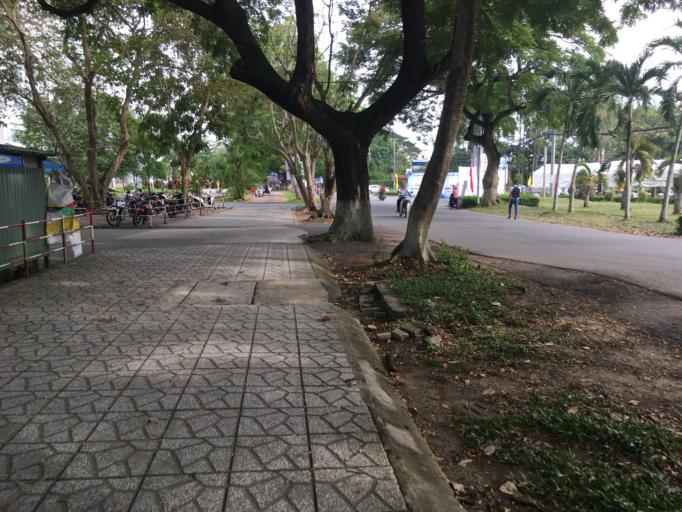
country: VN
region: Can Tho
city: Can Tho
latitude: 10.0301
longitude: 105.7694
